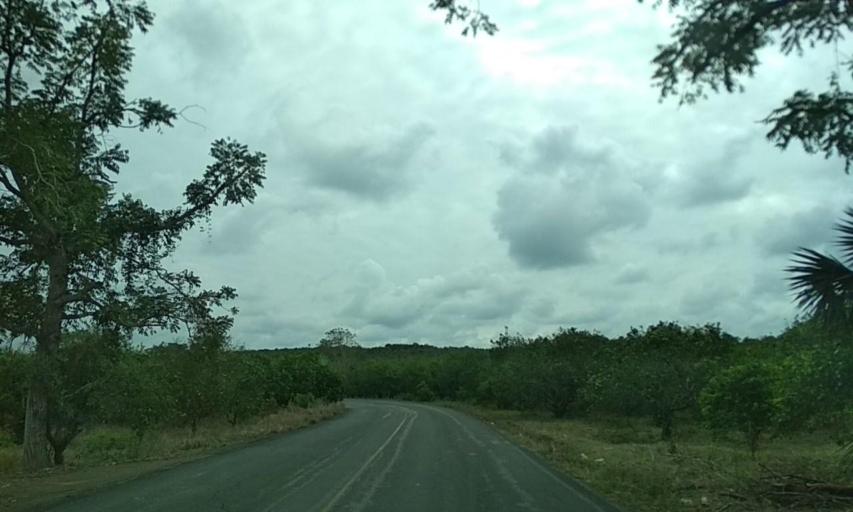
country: MX
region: Veracruz
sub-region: Papantla
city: El Chote
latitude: 20.3540
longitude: -97.3583
